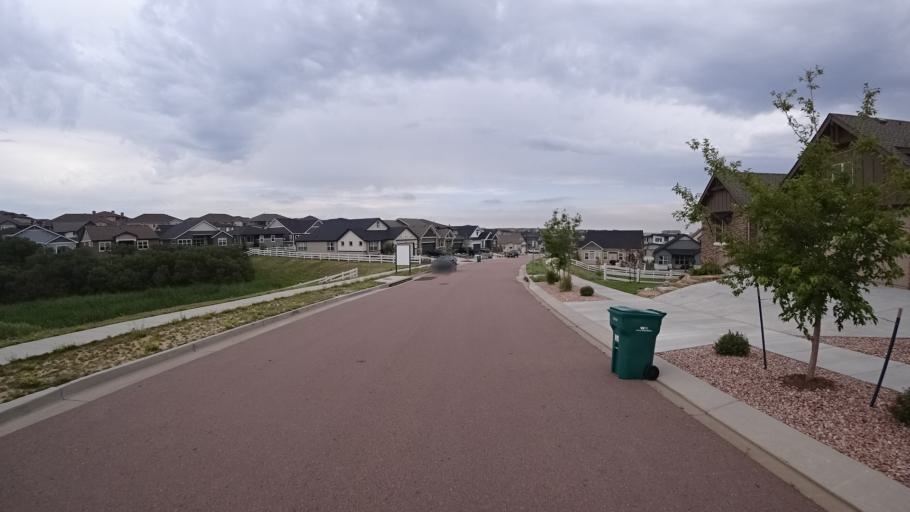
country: US
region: Colorado
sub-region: El Paso County
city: Gleneagle
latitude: 39.0034
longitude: -104.8048
